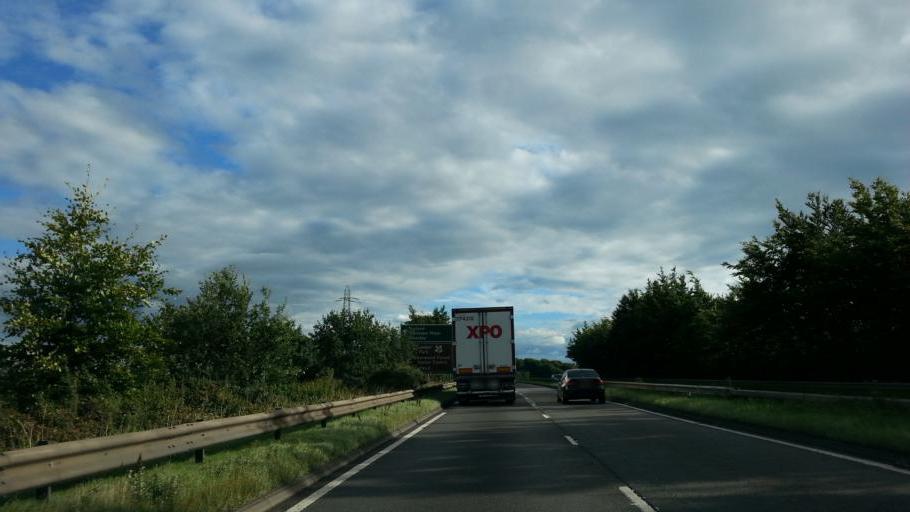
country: GB
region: England
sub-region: Nottinghamshire
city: Babworth
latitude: 53.3046
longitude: -1.0310
